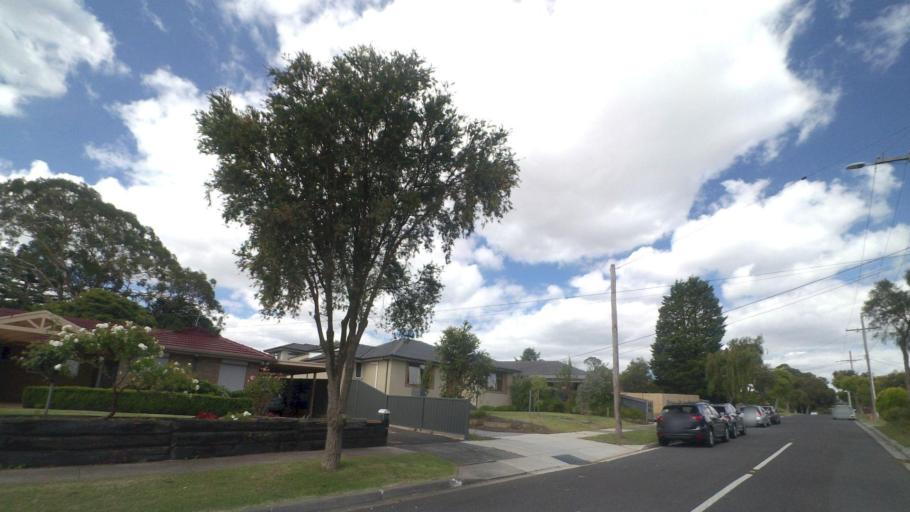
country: AU
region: Victoria
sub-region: Knox
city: Bayswater
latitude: -37.8633
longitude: 145.2543
